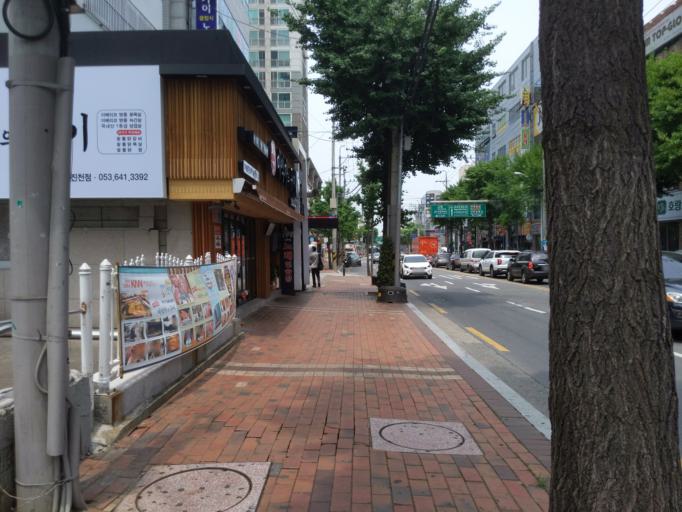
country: KR
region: Daegu
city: Hwawon
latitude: 35.8131
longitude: 128.5246
